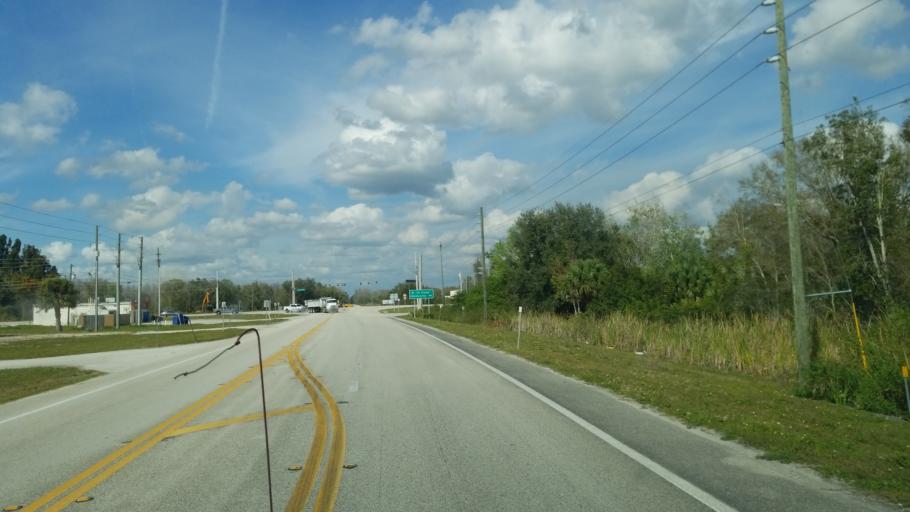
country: US
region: Florida
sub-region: Osceola County
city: Saint Cloud
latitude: 28.1433
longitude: -81.0761
